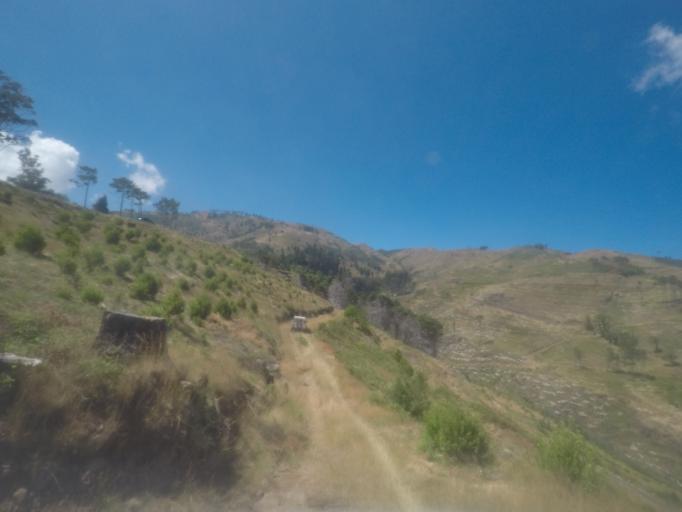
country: PT
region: Madeira
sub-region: Funchal
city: Nossa Senhora do Monte
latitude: 32.6941
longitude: -16.9034
